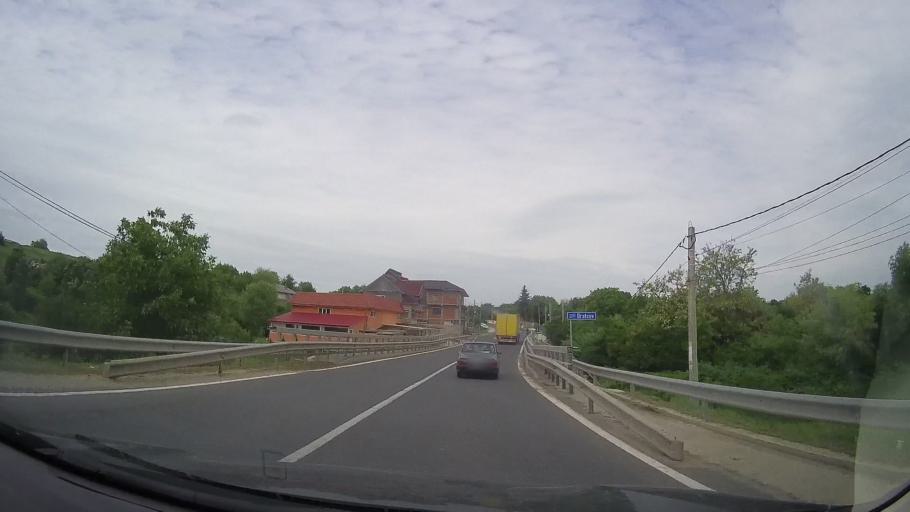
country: RO
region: Teleorman
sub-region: Comuna Maldaeni
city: Maldaeni
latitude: 44.1198
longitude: 24.9293
